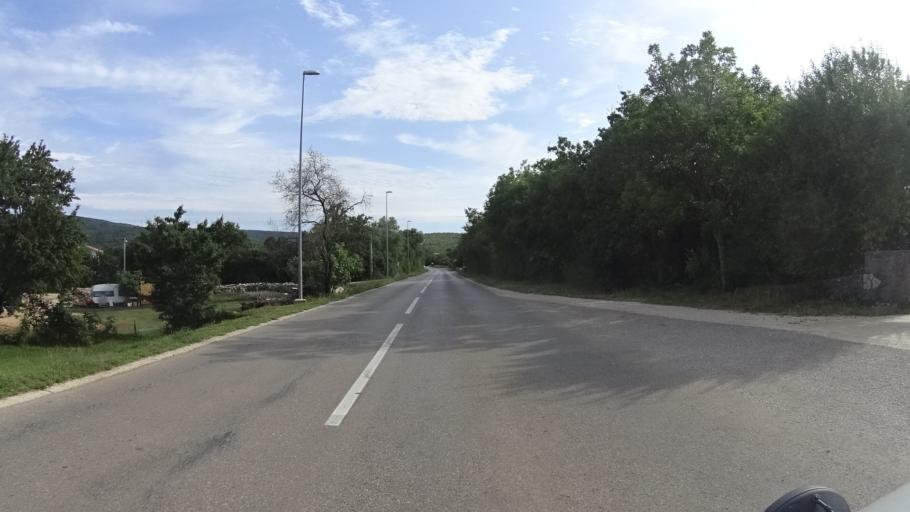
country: HR
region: Istarska
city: Rasa
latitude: 45.0787
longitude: 14.0967
